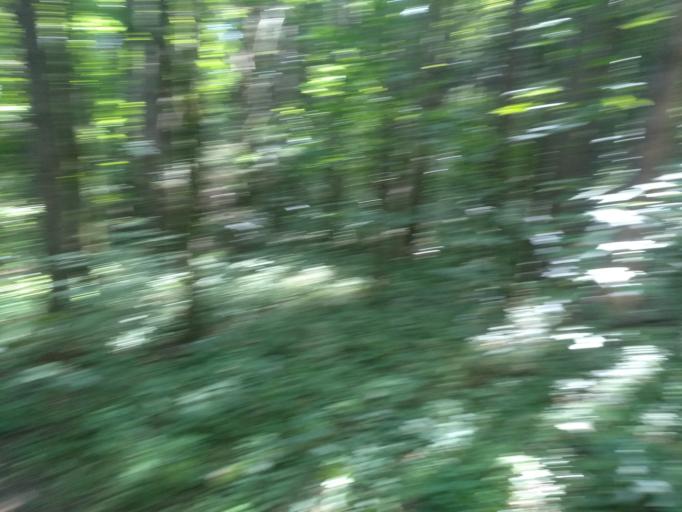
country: RU
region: Moskovskaya
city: Dedovsk
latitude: 55.8737
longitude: 37.0915
